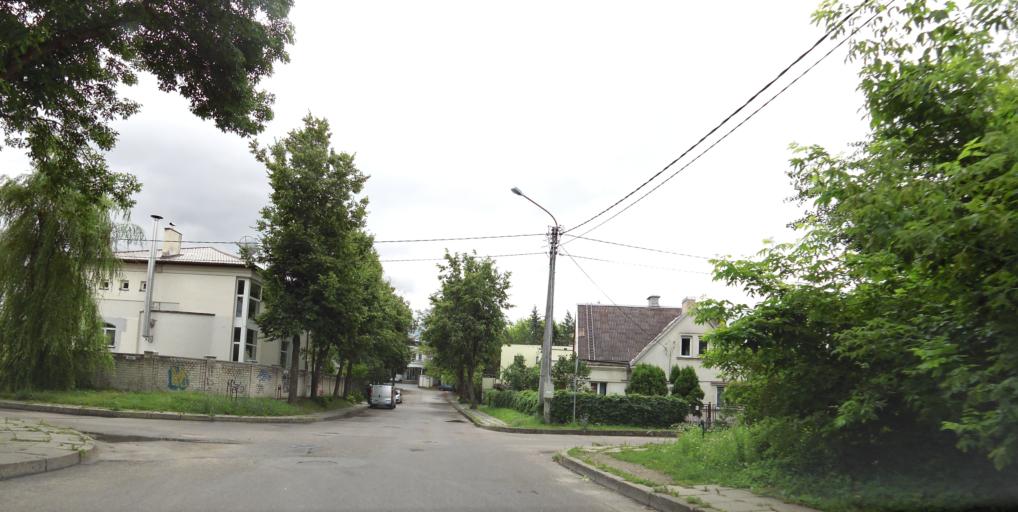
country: LT
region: Vilnius County
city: Seskine
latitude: 54.6957
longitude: 25.2464
